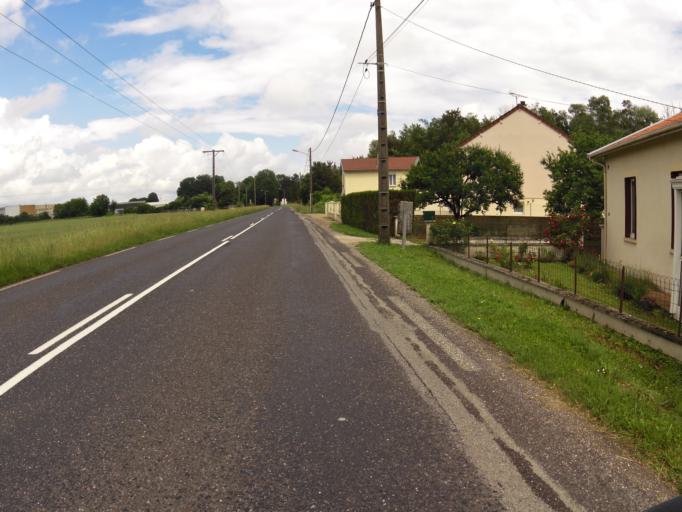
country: FR
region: Lorraine
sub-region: Departement de la Meuse
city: Revigny-sur-Ornain
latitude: 48.8152
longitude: 4.9752
